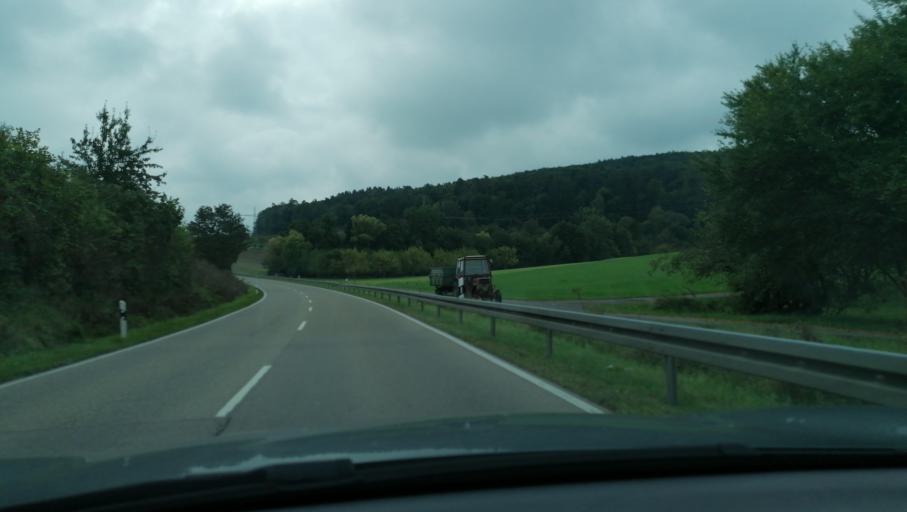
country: DE
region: Baden-Wuerttemberg
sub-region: Regierungsbezirk Stuttgart
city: Winnenden
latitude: 48.8625
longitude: 9.4251
